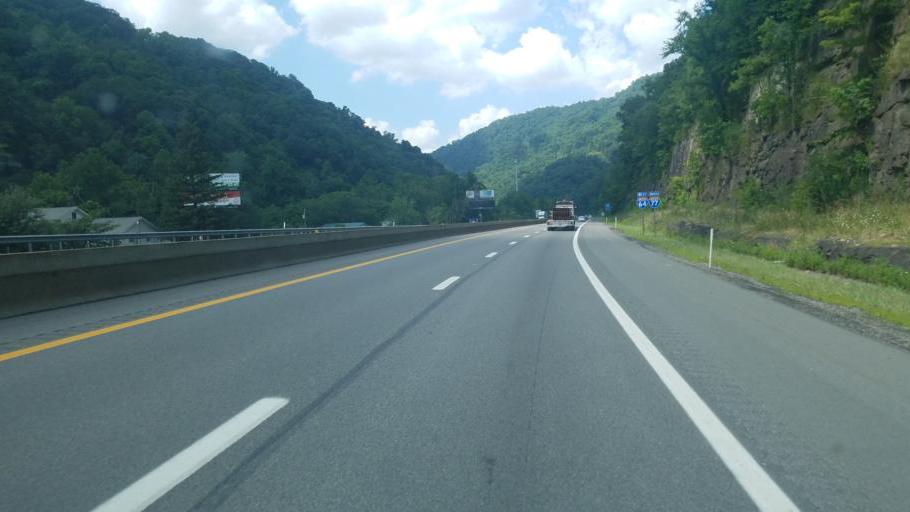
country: US
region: West Virginia
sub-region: Kanawha County
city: Montgomery
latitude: 38.0350
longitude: -81.3618
